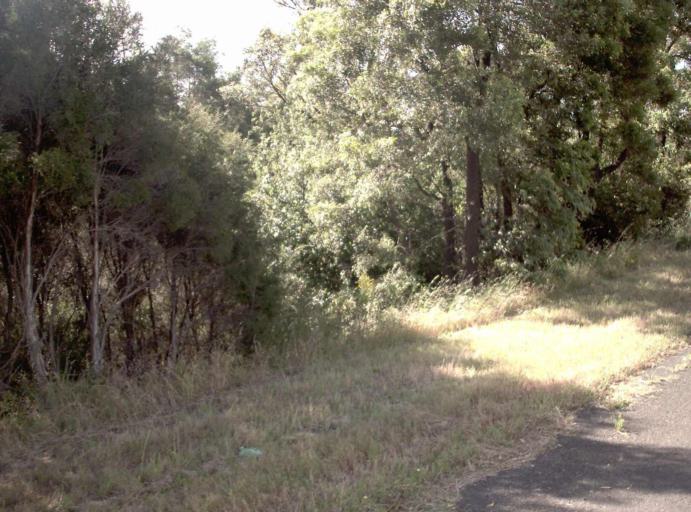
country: AU
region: Victoria
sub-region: Latrobe
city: Morwell
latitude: -38.1728
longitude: 146.4062
